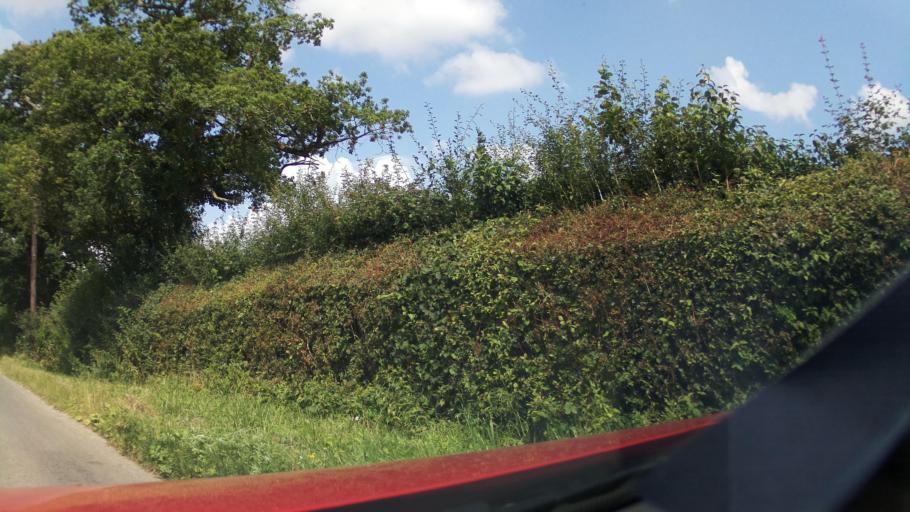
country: GB
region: England
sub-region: Wiltshire
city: Malmesbury
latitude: 51.5604
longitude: -2.1168
